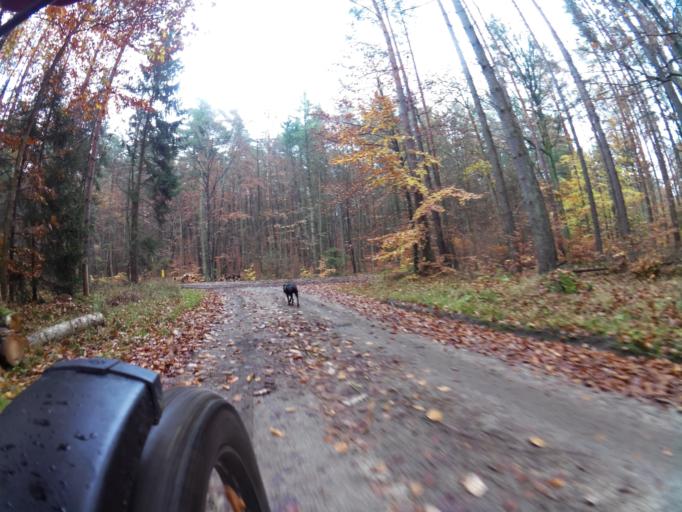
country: PL
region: Pomeranian Voivodeship
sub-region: Powiat pucki
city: Krokowa
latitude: 54.7469
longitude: 18.0957
